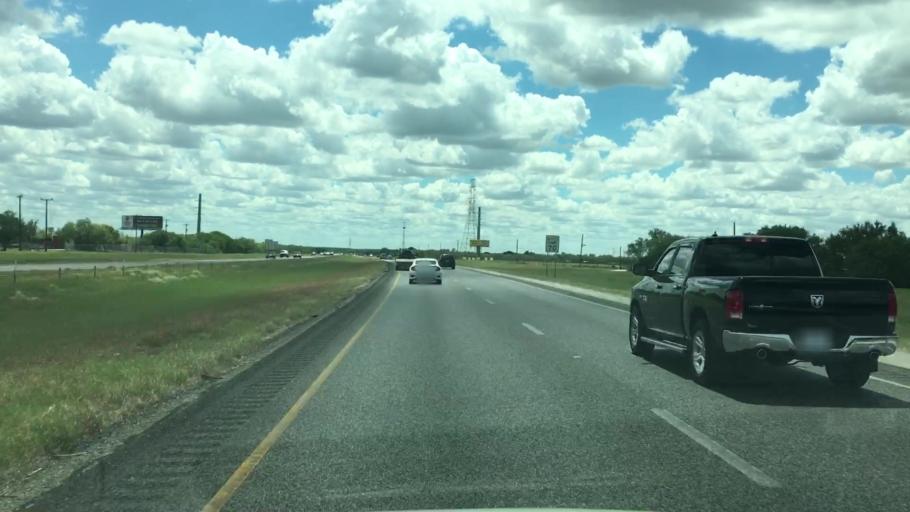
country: US
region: Texas
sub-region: Bexar County
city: Elmendorf
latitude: 29.2733
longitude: -98.3963
